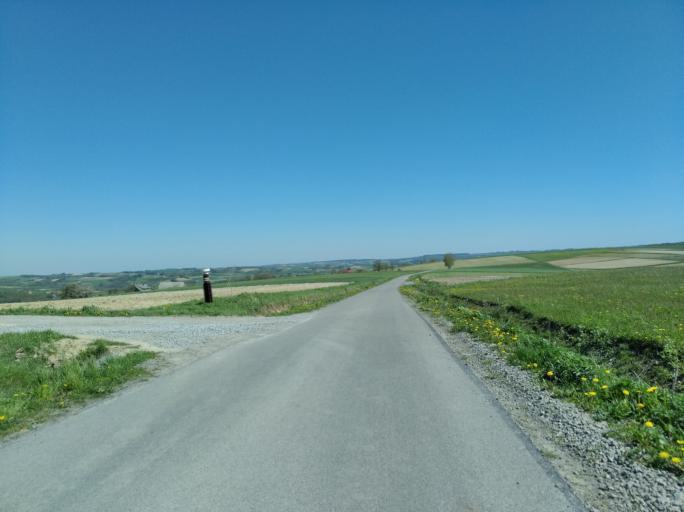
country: PL
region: Subcarpathian Voivodeship
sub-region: Powiat ropczycko-sedziszowski
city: Wielopole Skrzynskie
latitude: 49.9056
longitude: 21.5512
